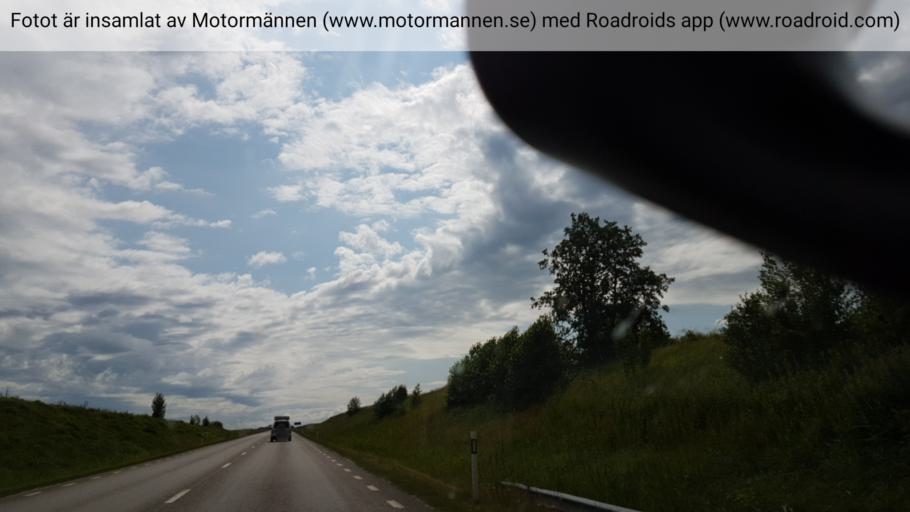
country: SE
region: Vaestra Goetaland
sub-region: Vara Kommun
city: Vara
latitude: 58.2979
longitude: 12.9388
